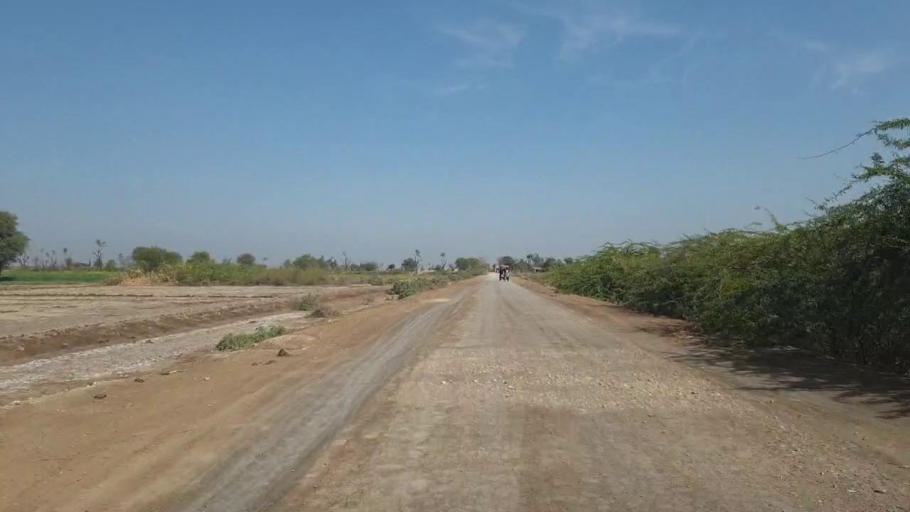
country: PK
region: Sindh
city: Samaro
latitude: 25.3370
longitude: 69.2476
